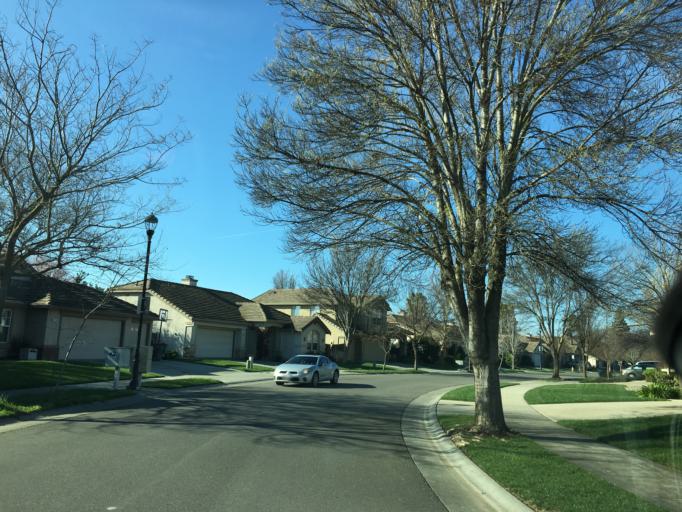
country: US
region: California
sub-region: Yolo County
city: Davis
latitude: 38.5560
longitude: -121.6992
